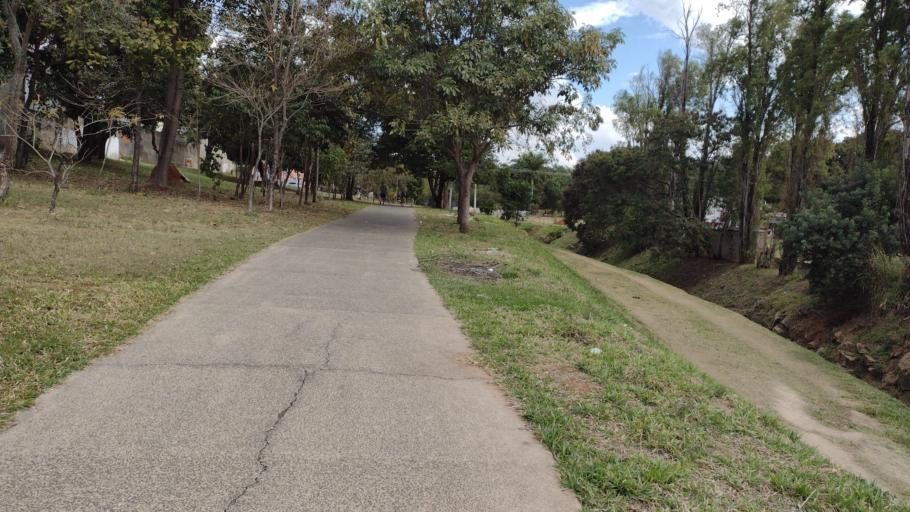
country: BR
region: Sao Paulo
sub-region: Sorocaba
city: Sorocaba
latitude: -23.4604
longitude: -47.4714
